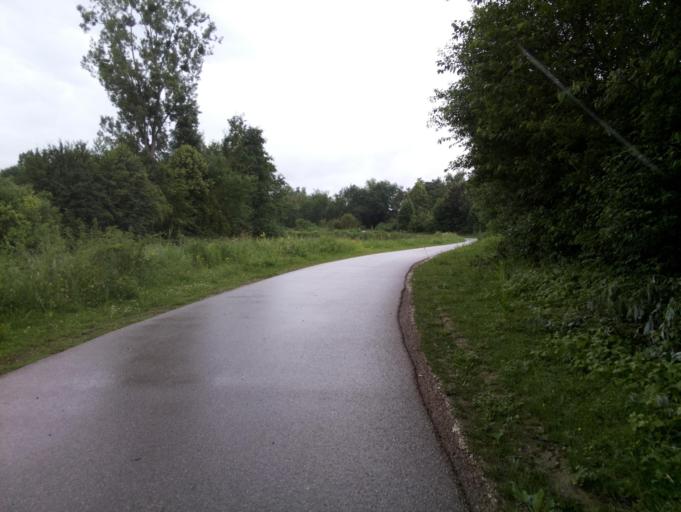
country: FR
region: Picardie
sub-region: Departement de la Somme
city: Ailly-sur-Somme
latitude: 49.9371
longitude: 2.1806
